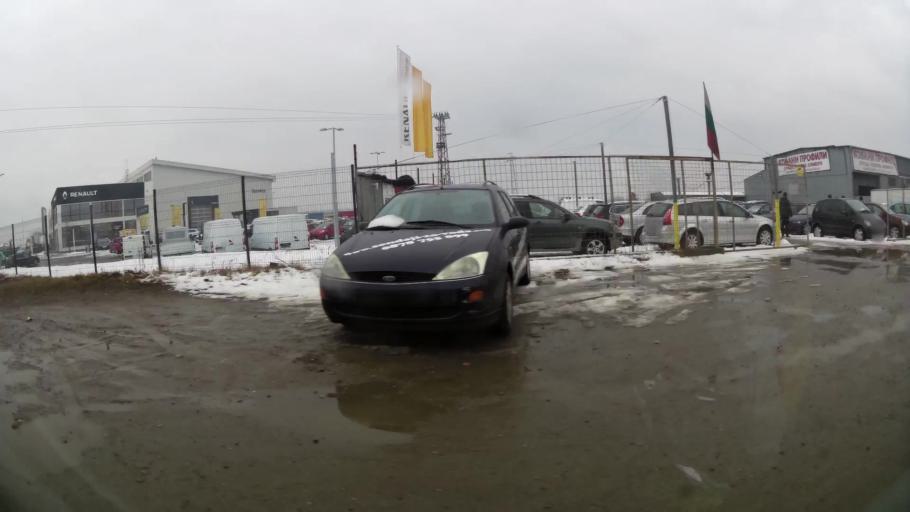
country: BG
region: Sofiya
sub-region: Obshtina Bozhurishte
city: Bozhurishte
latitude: 42.6944
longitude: 23.2303
